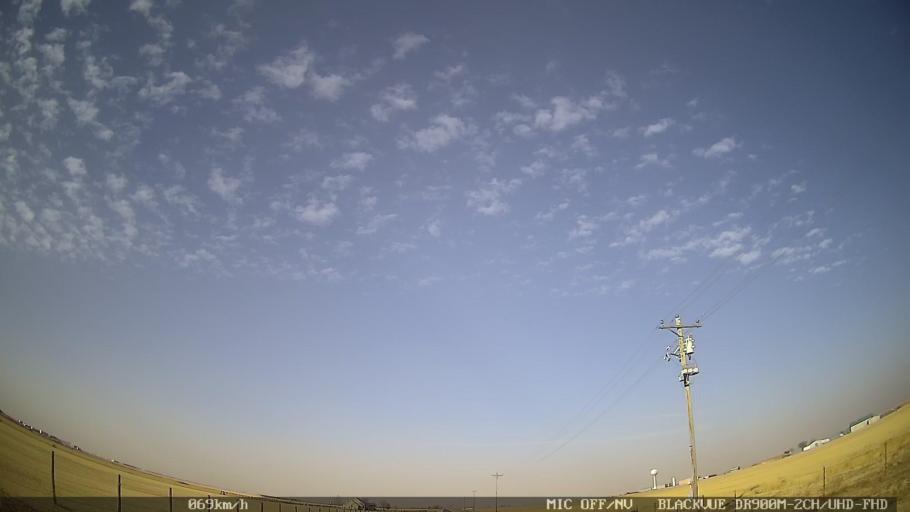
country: US
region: New Mexico
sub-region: Curry County
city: Texico
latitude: 34.4213
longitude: -103.0907
